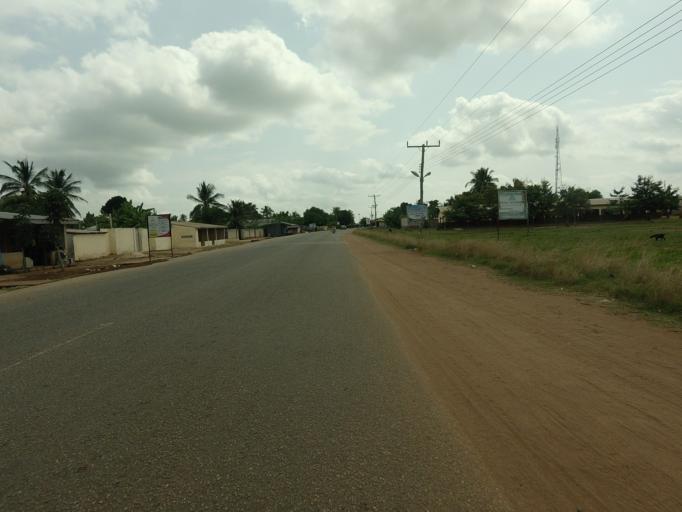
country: TG
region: Maritime
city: Lome
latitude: 6.2217
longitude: 1.0364
